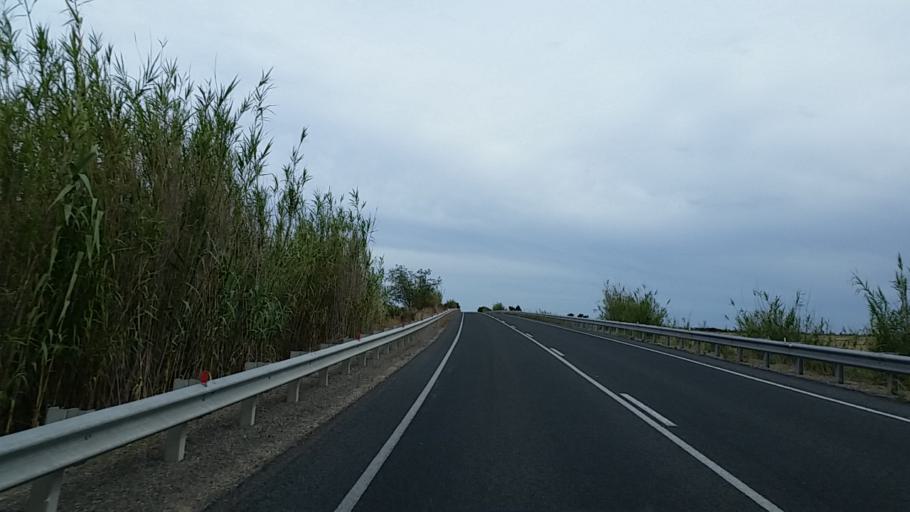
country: AU
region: South Australia
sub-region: Murray Bridge
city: Murray Bridge
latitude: -35.1380
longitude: 139.3274
